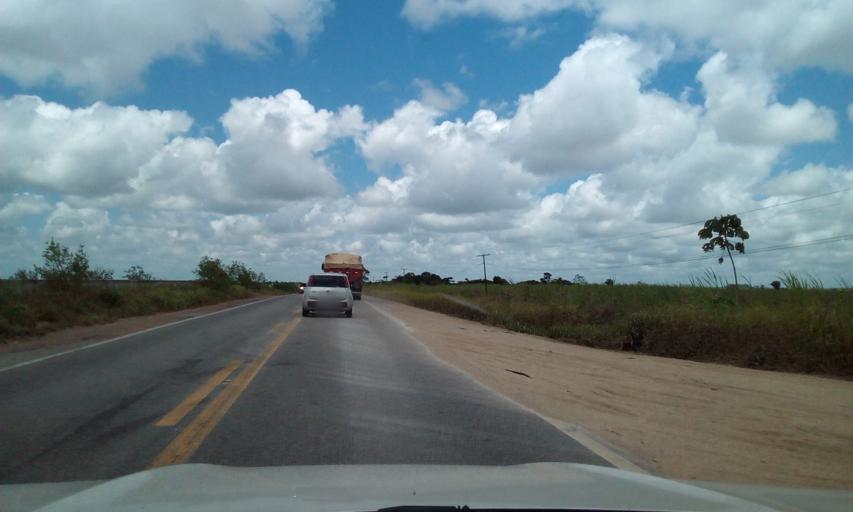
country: BR
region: Alagoas
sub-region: Sao Miguel Dos Campos
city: Sao Miguel dos Campos
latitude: -9.8333
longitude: -36.1310
